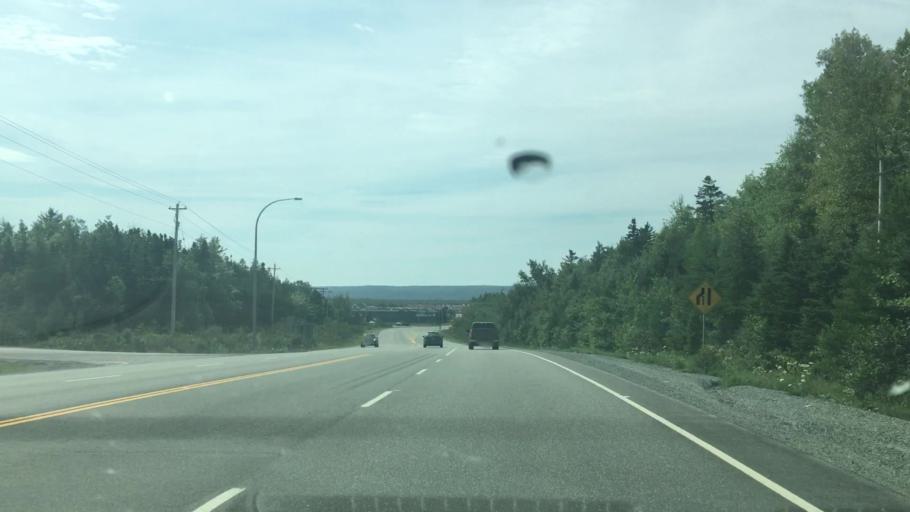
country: CA
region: Nova Scotia
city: Port Hawkesbury
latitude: 45.6245
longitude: -61.3328
